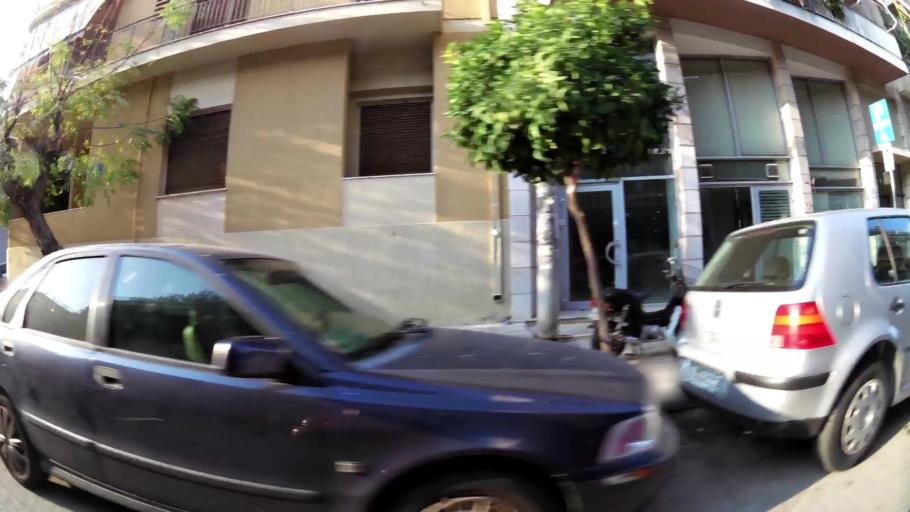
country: GR
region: Attica
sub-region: Nomarchia Athinas
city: Dhafni
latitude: 37.9493
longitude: 23.7359
